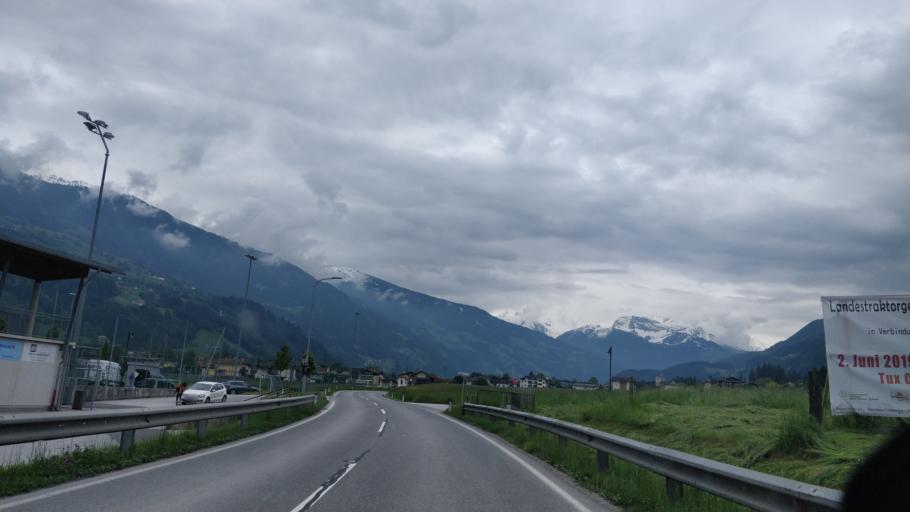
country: AT
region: Tyrol
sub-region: Politischer Bezirk Schwaz
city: Ried im Zillertal
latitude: 47.3065
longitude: 11.8689
